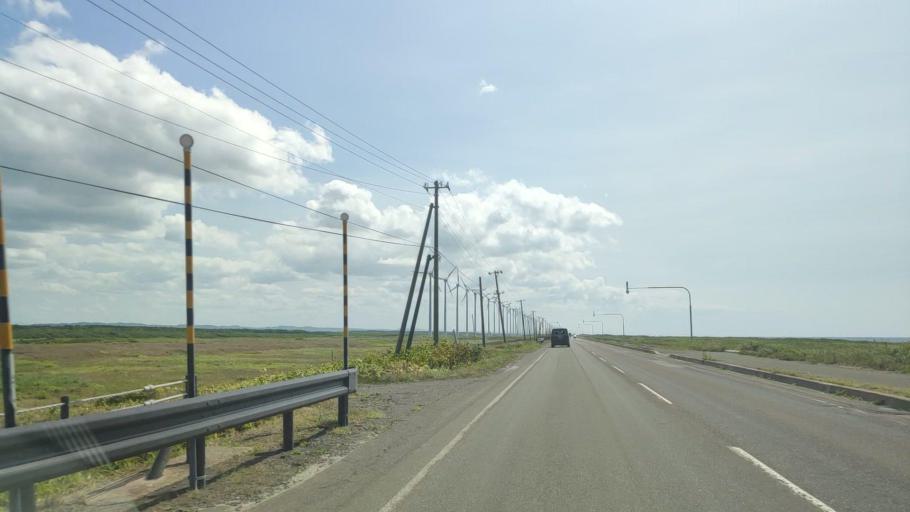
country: JP
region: Hokkaido
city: Makubetsu
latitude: 44.9883
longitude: 141.6892
